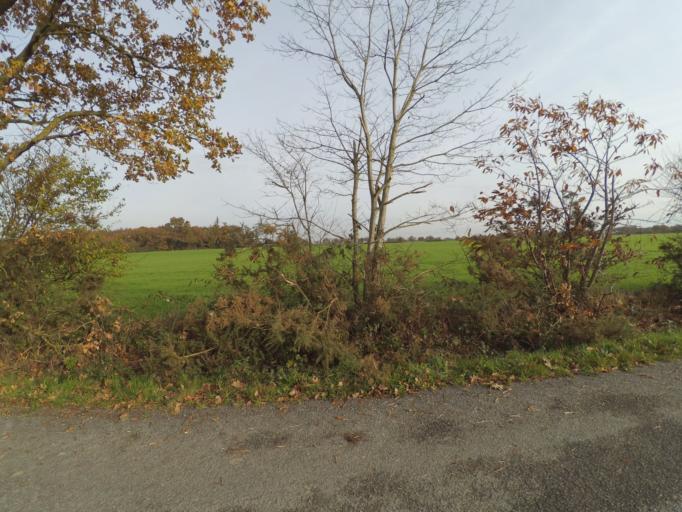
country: FR
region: Pays de la Loire
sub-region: Departement de la Loire-Atlantique
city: La Planche
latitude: 47.0143
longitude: -1.3956
